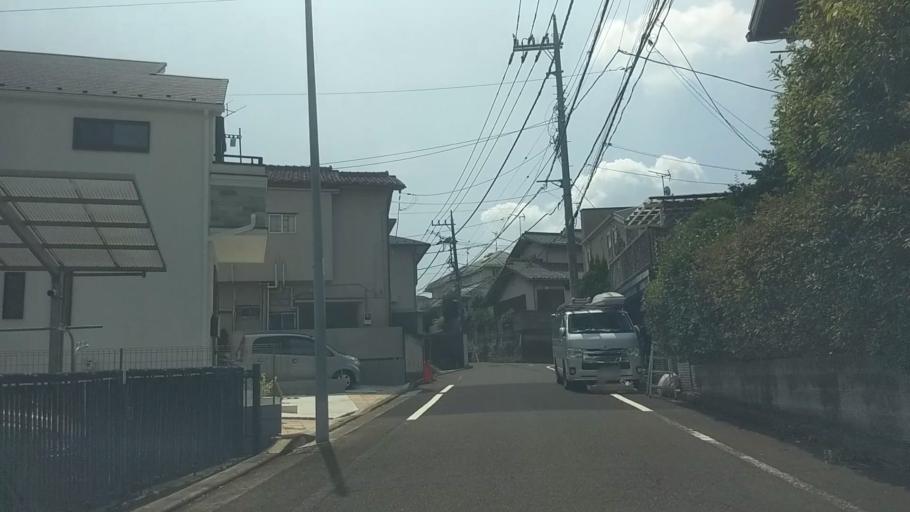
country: JP
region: Kanagawa
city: Yokohama
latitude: 35.5127
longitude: 139.6484
